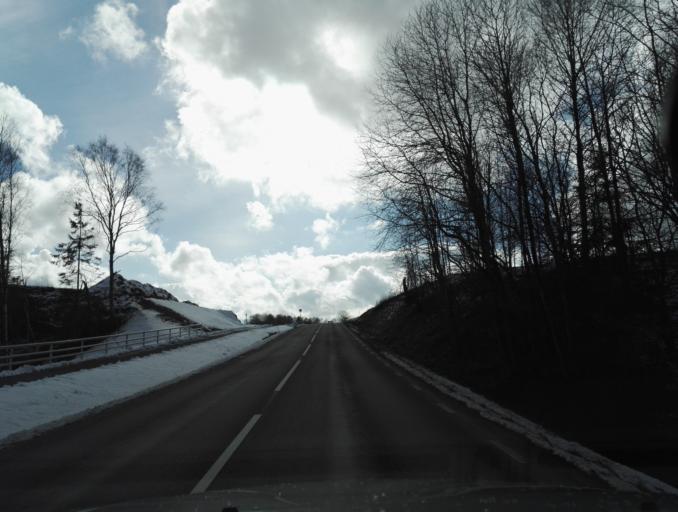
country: SE
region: Vaestra Goetaland
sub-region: Bollebygds Kommun
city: Bollebygd
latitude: 57.6893
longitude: 12.5686
